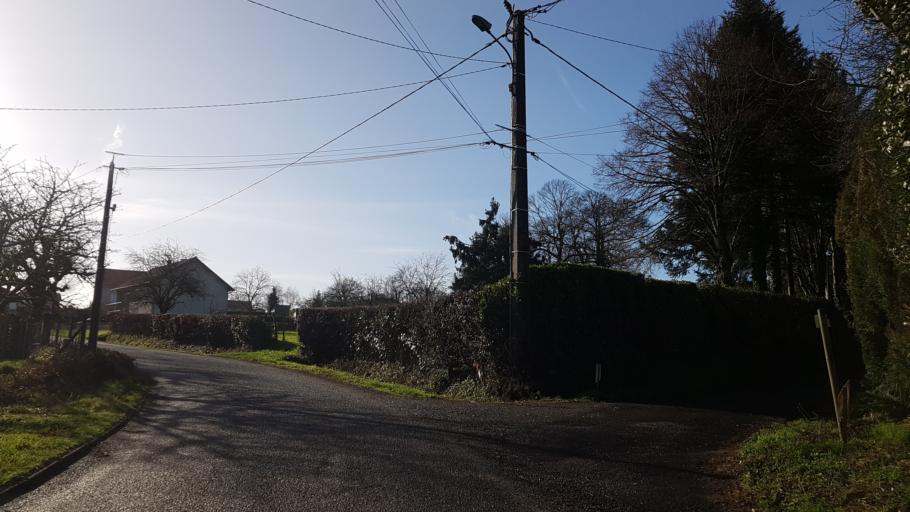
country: FR
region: Poitou-Charentes
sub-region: Departement de la Charente
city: Etagnac
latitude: 45.8969
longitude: 0.8008
